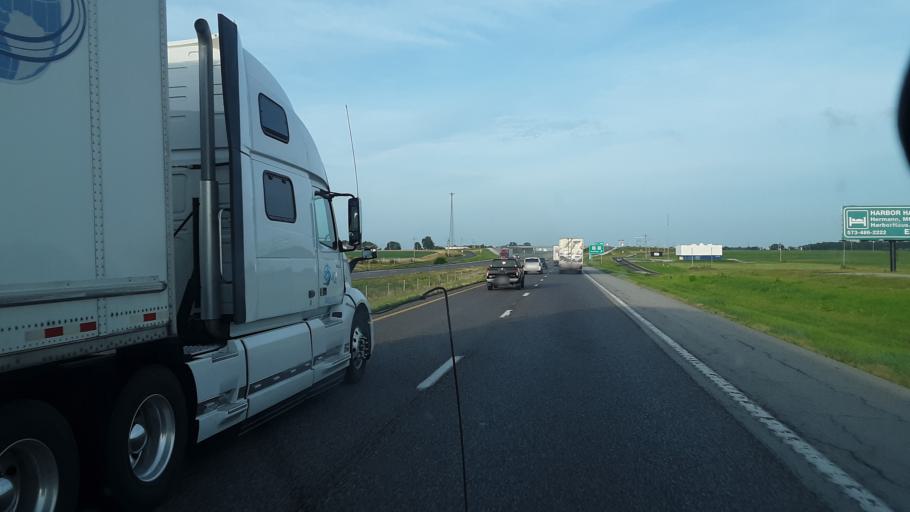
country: US
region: Missouri
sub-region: Callaway County
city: Fulton
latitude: 38.9519
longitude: -92.0162
